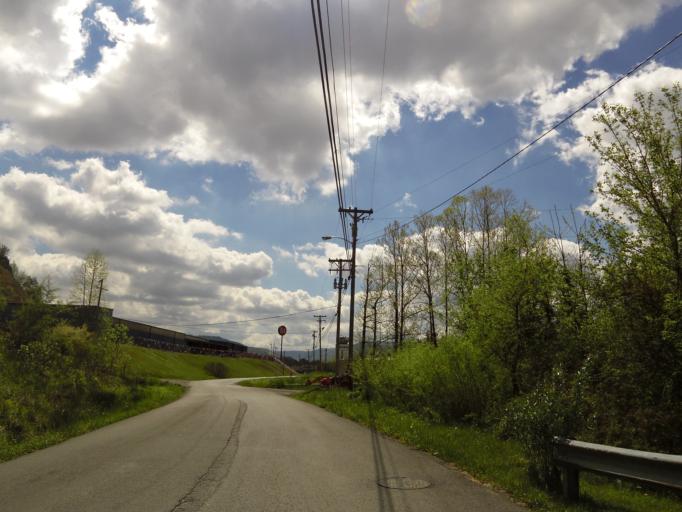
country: US
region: Kentucky
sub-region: Bell County
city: Middlesboro
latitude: 36.6255
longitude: -83.7012
